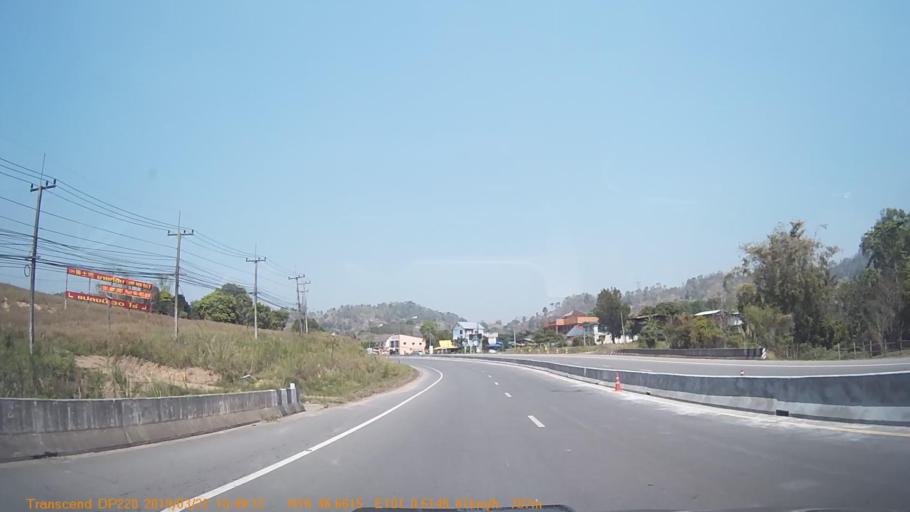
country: TH
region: Phetchabun
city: Khao Kho
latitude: 16.7779
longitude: 101.0083
